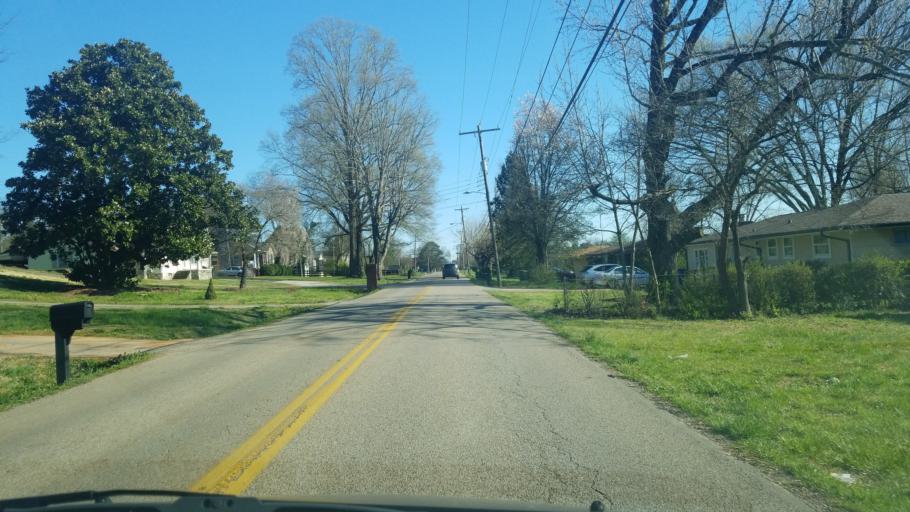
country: US
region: Tennessee
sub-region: Hamilton County
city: East Brainerd
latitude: 35.0215
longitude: -85.1796
